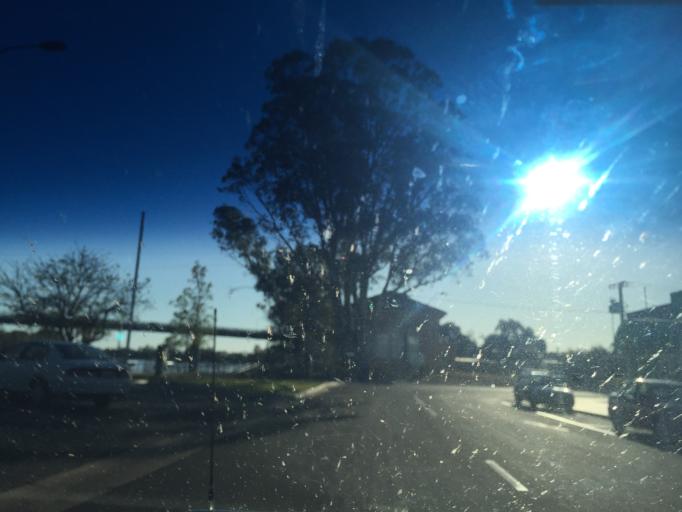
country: AU
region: South Australia
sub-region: Berri and Barmera
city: Berri
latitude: -34.2881
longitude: 140.6012
